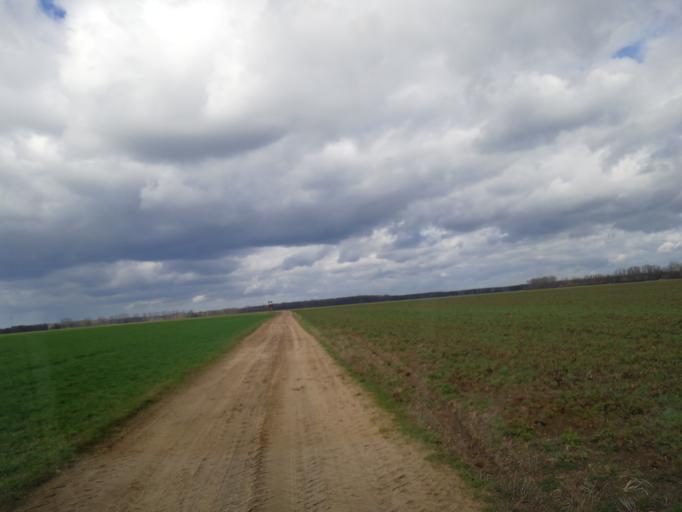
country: DE
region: Brandenburg
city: Schonewalde
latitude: 51.6813
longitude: 13.5567
